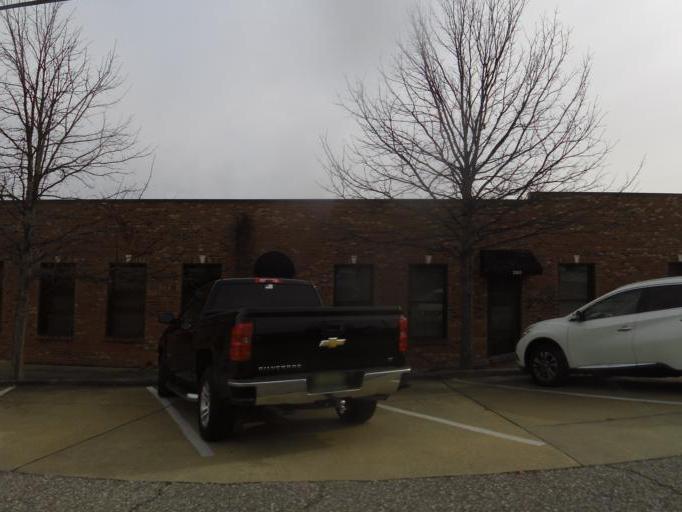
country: US
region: Alabama
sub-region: Montgomery County
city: Montgomery
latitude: 32.3773
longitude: -86.3153
